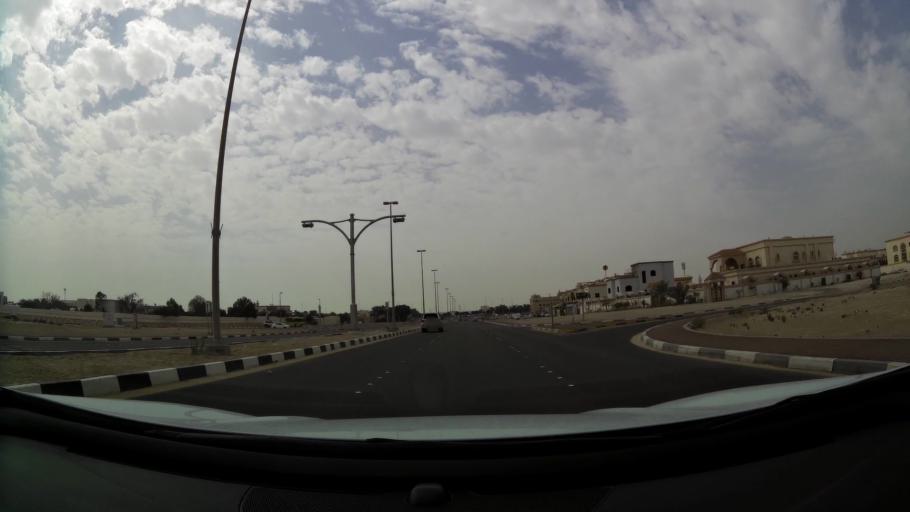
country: AE
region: Abu Dhabi
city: Abu Dhabi
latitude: 24.2988
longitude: 54.6319
